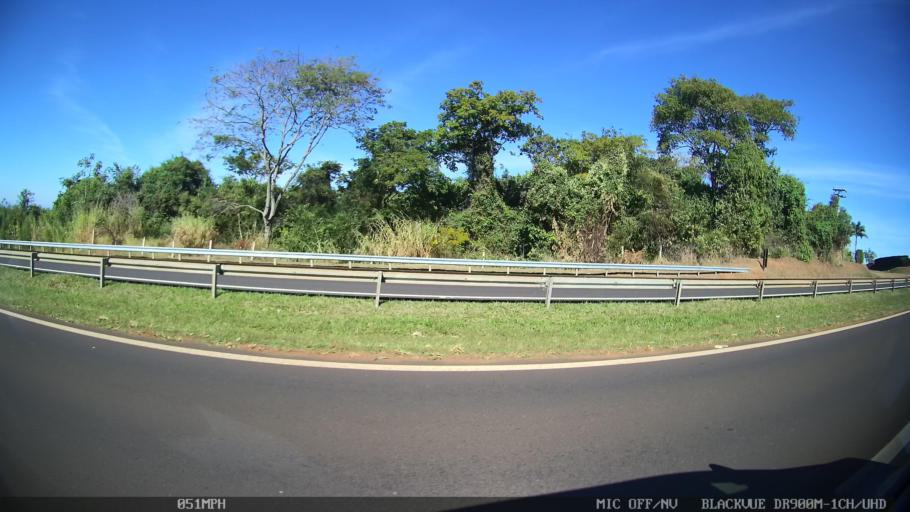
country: BR
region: Sao Paulo
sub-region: Franca
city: Franca
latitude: -20.5777
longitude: -47.3456
